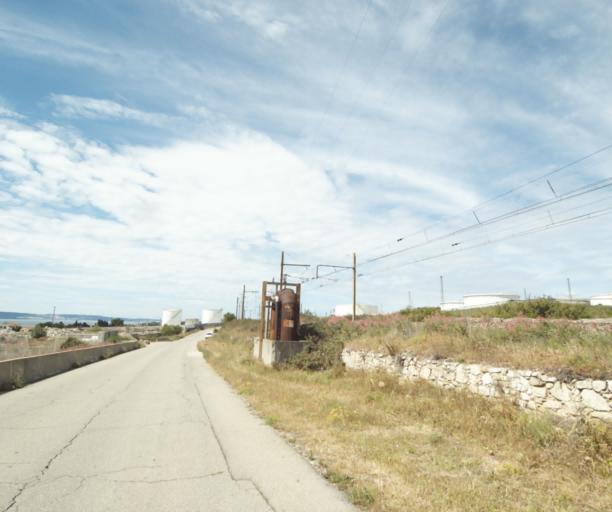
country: FR
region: Provence-Alpes-Cote d'Azur
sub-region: Departement des Bouches-du-Rhone
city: Rognac
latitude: 43.4943
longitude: 5.2029
